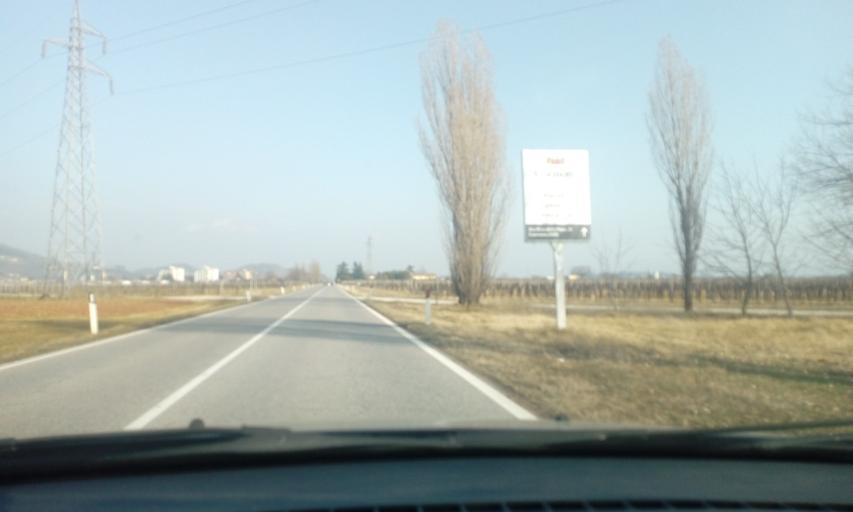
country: IT
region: Friuli Venezia Giulia
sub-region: Provincia di Gorizia
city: Cormons
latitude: 45.9527
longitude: 13.4485
